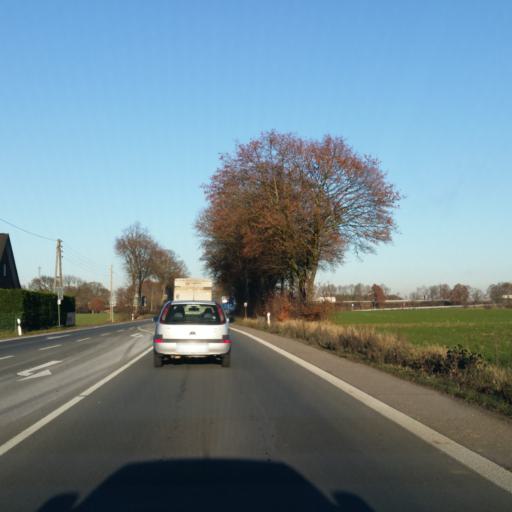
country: DE
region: North Rhine-Westphalia
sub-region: Regierungsbezirk Munster
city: Isselburg
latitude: 51.8129
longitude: 6.4379
